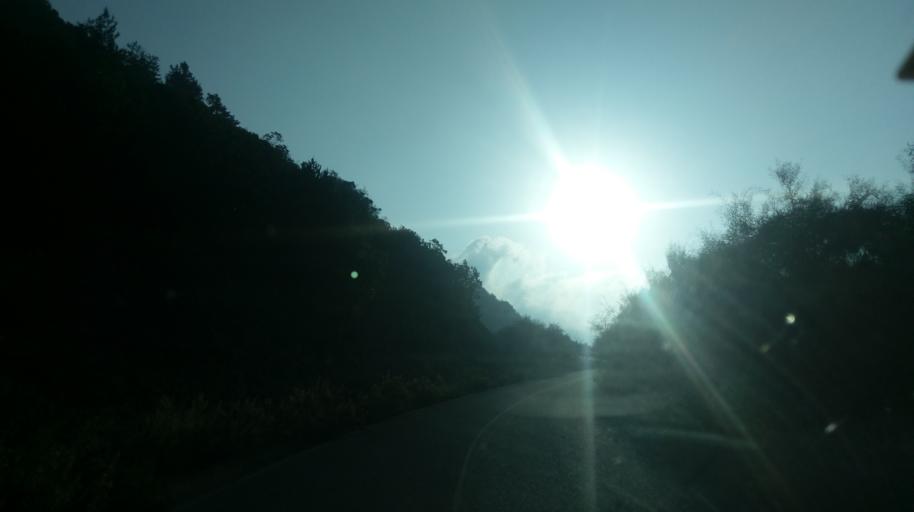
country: CY
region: Ammochostos
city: Trikomo
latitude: 35.4007
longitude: 33.9037
